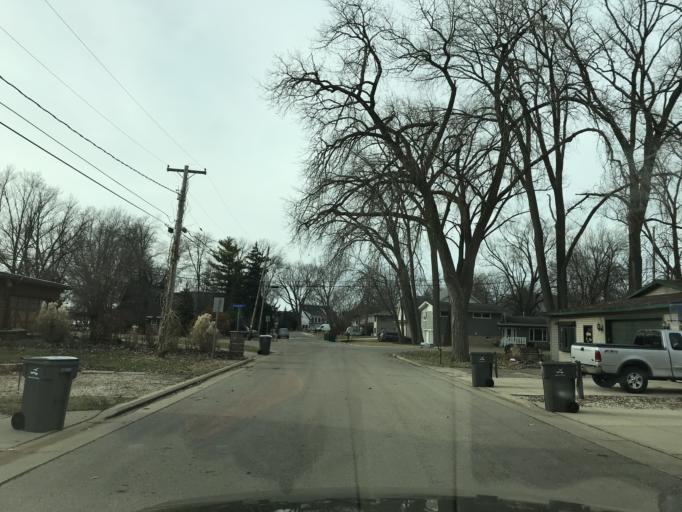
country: US
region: Wisconsin
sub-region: Dane County
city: Monona
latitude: 43.0560
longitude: -89.3456
